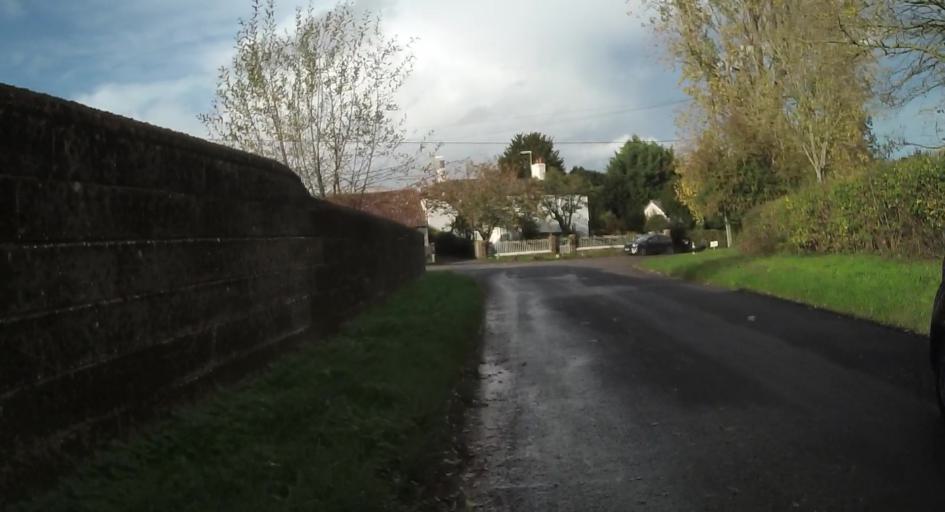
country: GB
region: England
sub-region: Hampshire
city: Kingsley
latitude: 51.1767
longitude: -0.8938
